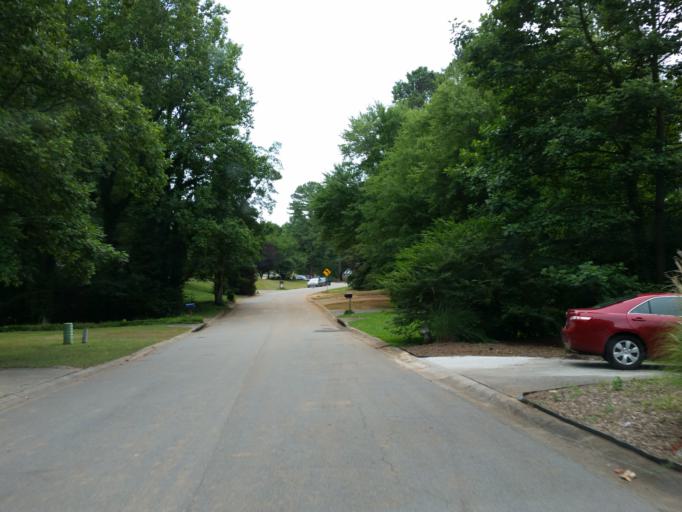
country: US
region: Georgia
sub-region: Cherokee County
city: Woodstock
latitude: 34.0176
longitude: -84.4779
